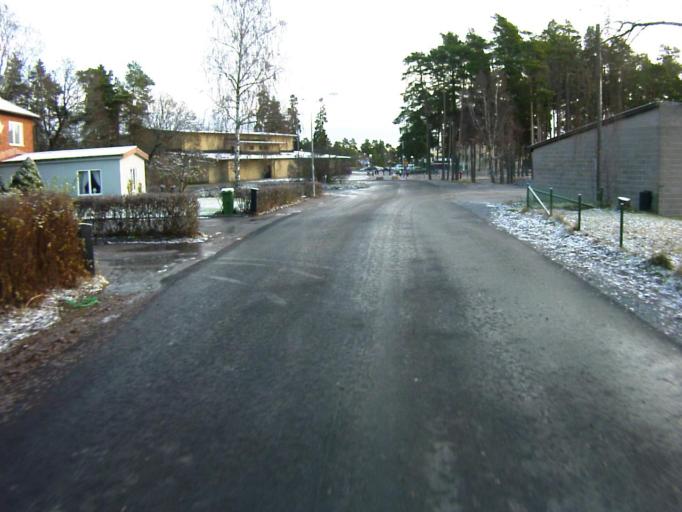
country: SE
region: Soedermanland
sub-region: Eskilstuna Kommun
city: Hallbybrunn
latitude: 59.3923
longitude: 16.4221
